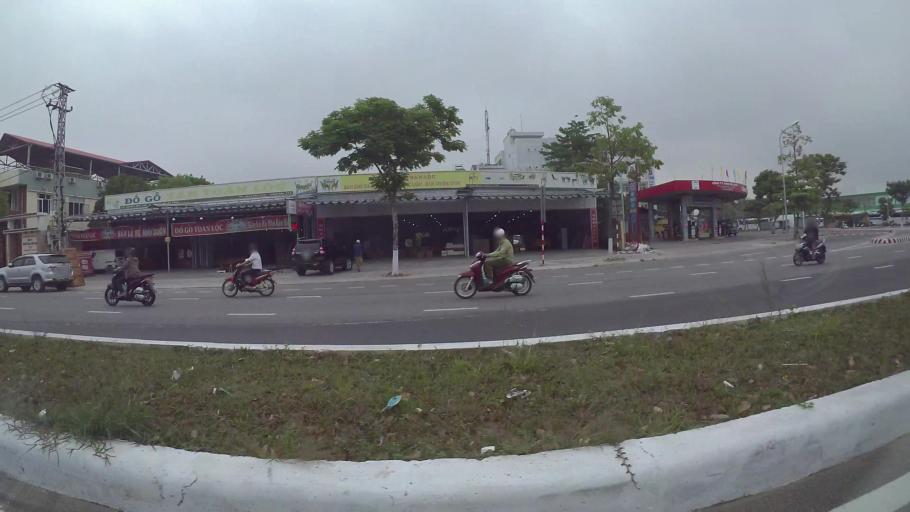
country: VN
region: Da Nang
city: Cam Le
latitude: 16.0253
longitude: 108.2089
